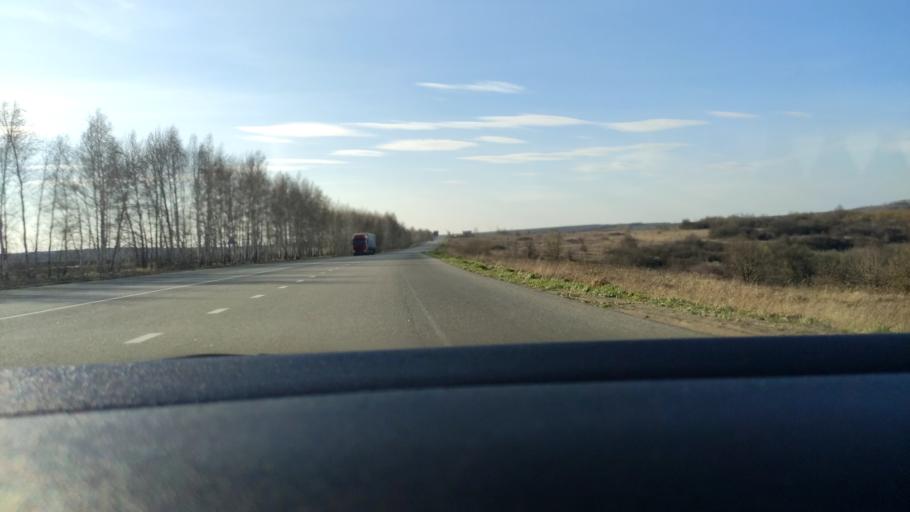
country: RU
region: Voronezj
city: Kolodeznyy
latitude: 51.3237
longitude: 39.1069
